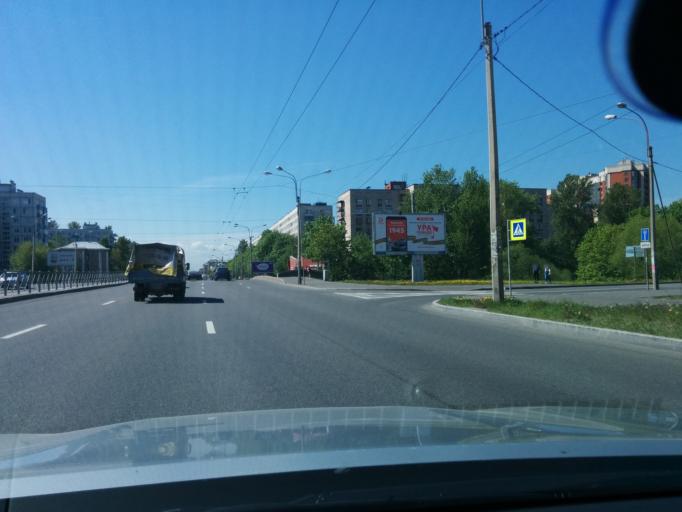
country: RU
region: St.-Petersburg
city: Krasnogvargeisky
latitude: 59.9324
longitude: 30.4295
